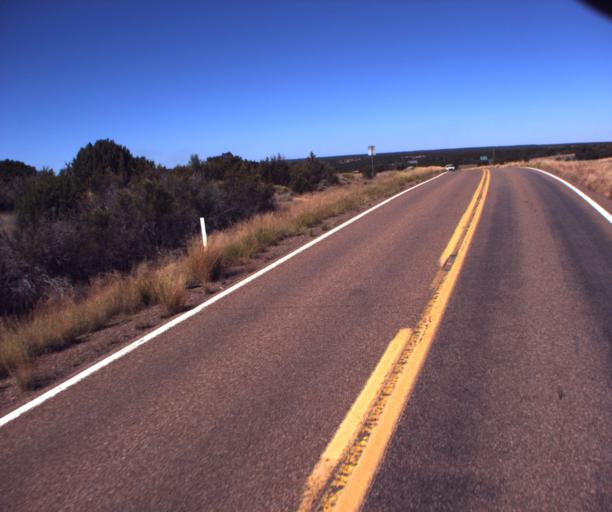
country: US
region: Arizona
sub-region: Navajo County
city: Heber-Overgaard
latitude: 34.4627
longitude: -110.4722
